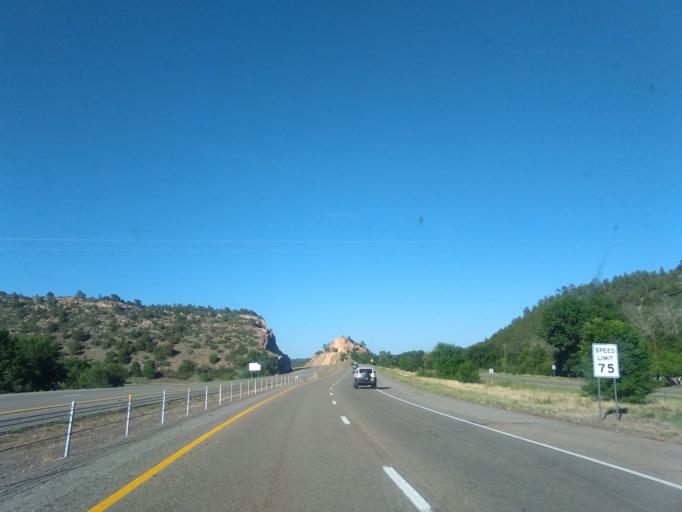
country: US
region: New Mexico
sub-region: San Miguel County
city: Las Vegas
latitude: 35.5244
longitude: -105.2443
